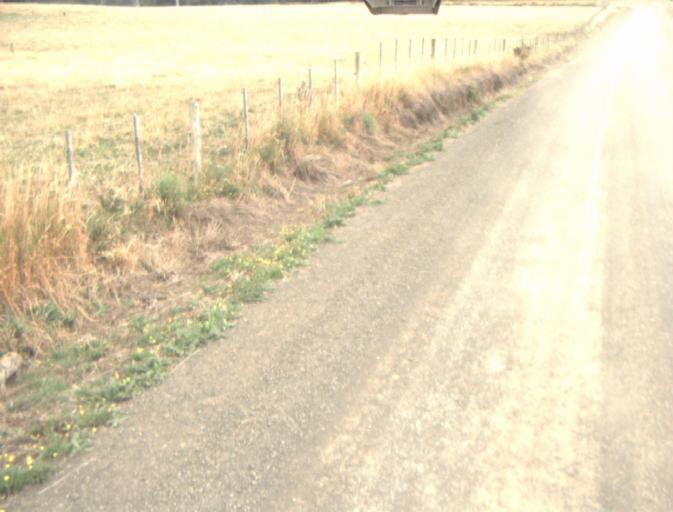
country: AU
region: Tasmania
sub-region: Northern Midlands
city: Evandale
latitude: -41.4657
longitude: 147.5361
